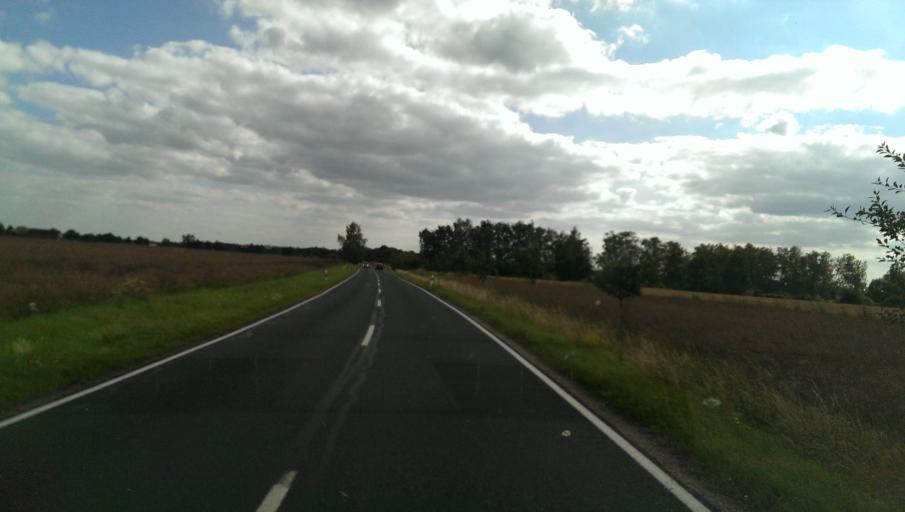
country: DE
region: Saxony-Anhalt
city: Worlitz
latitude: 51.8240
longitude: 12.4107
